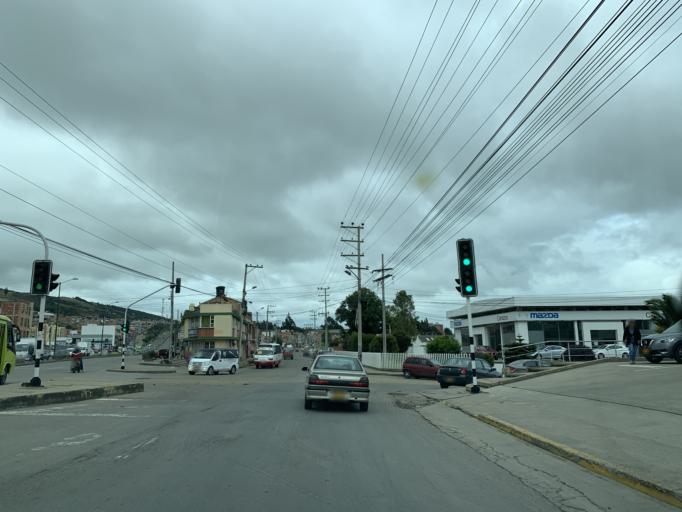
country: CO
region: Boyaca
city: Tunja
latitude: 5.5601
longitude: -73.3486
